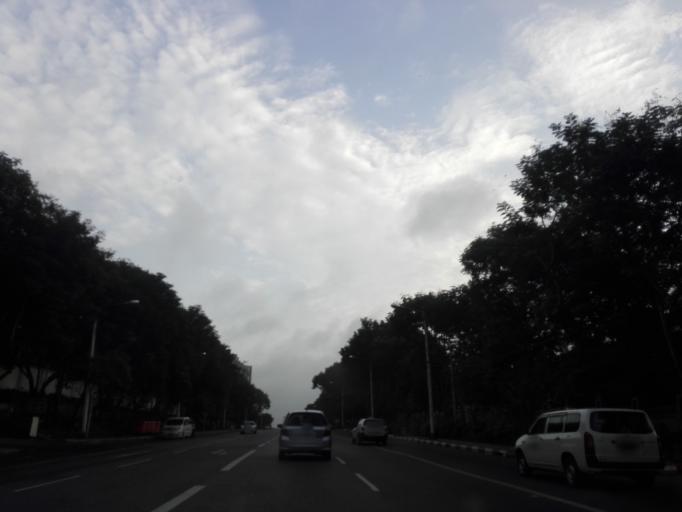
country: MM
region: Yangon
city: Yangon
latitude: 16.8545
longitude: 96.1410
